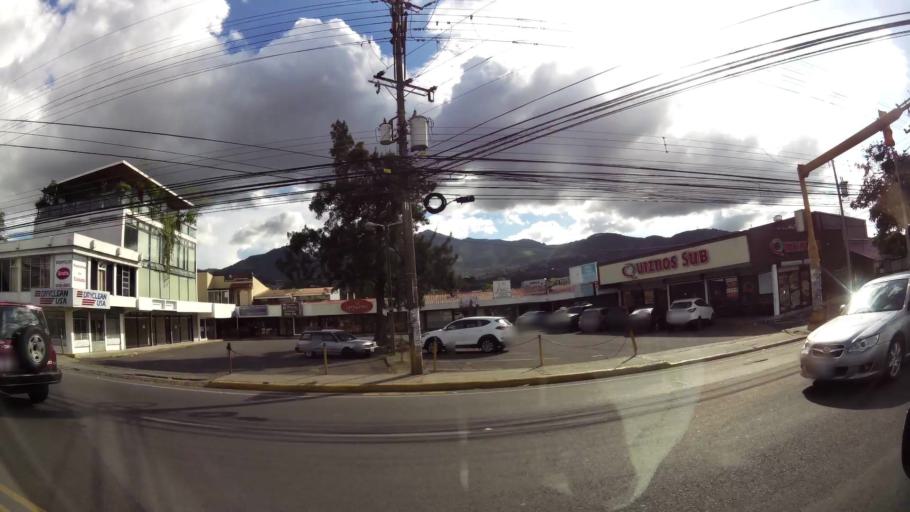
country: CR
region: San Jose
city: San Rafael
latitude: 9.9323
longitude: -84.1280
